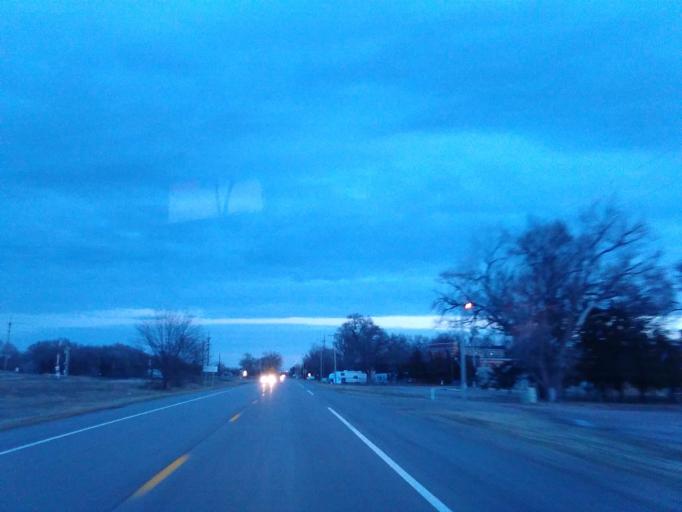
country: US
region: Nebraska
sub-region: Garden County
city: Oshkosh
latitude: 41.3354
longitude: -102.1520
